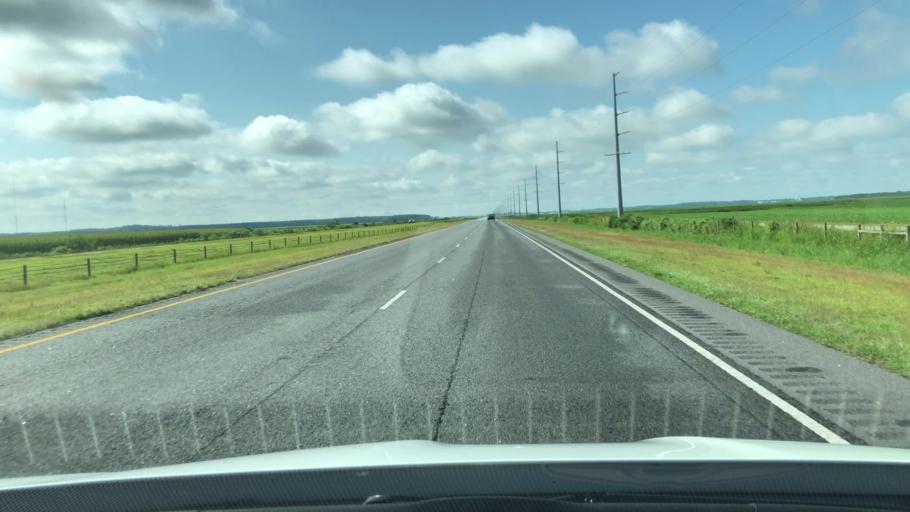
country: US
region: North Carolina
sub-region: Pasquotank County
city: Elizabeth City
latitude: 36.3299
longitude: -76.3115
